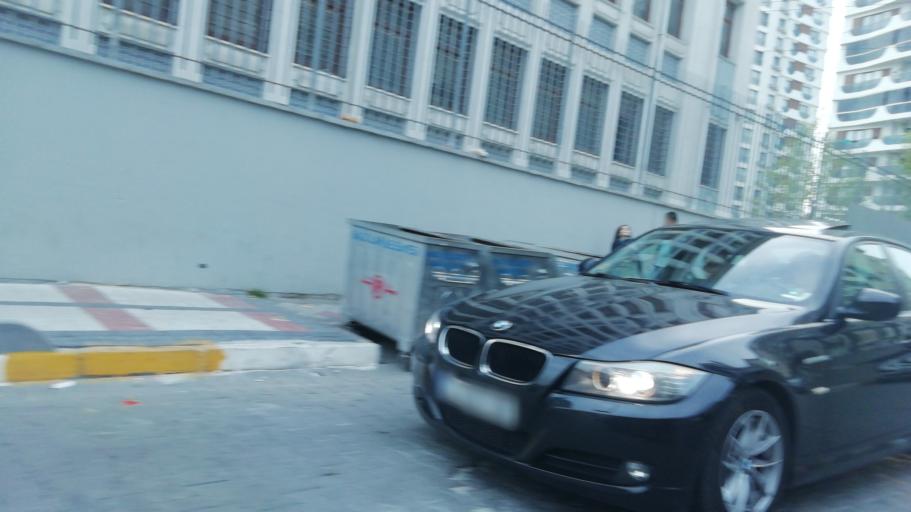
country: TR
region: Istanbul
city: Mahmutbey
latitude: 41.0301
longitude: 28.8331
